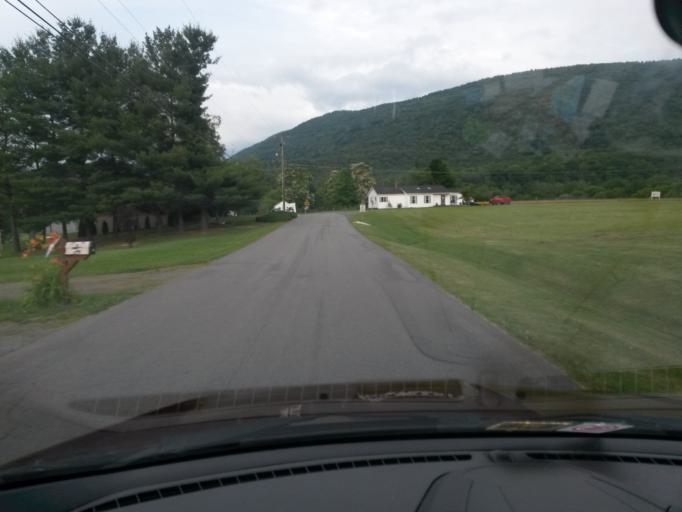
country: US
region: Virginia
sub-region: City of Covington
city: Fairlawn
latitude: 37.7667
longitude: -79.9686
